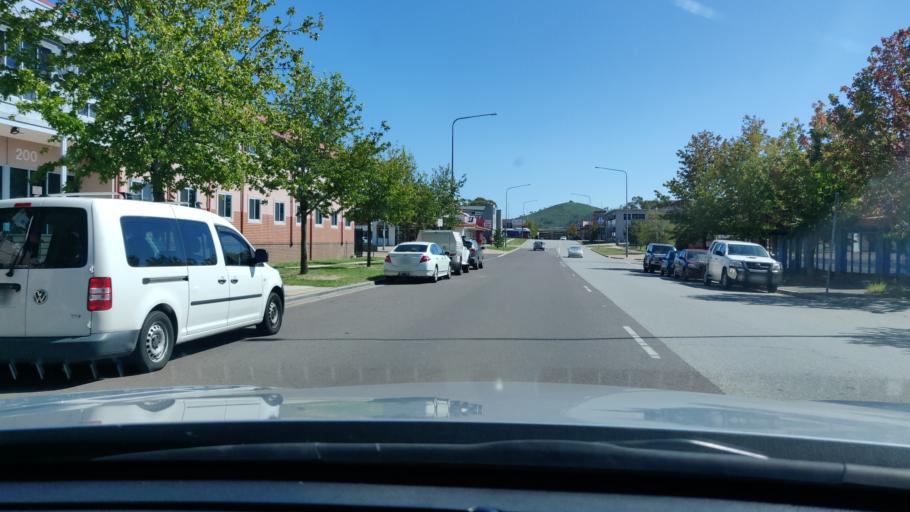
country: AU
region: Australian Capital Territory
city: Macarthur
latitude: -35.4209
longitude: 149.0685
